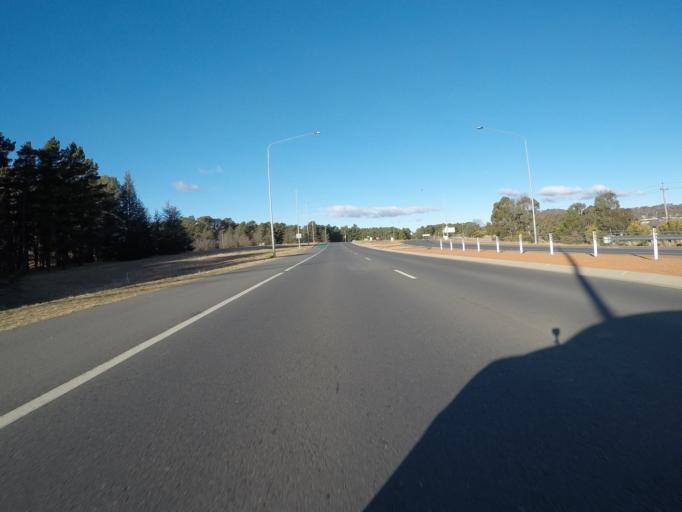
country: AU
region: Australian Capital Territory
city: Forrest
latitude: -35.3124
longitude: 149.0869
